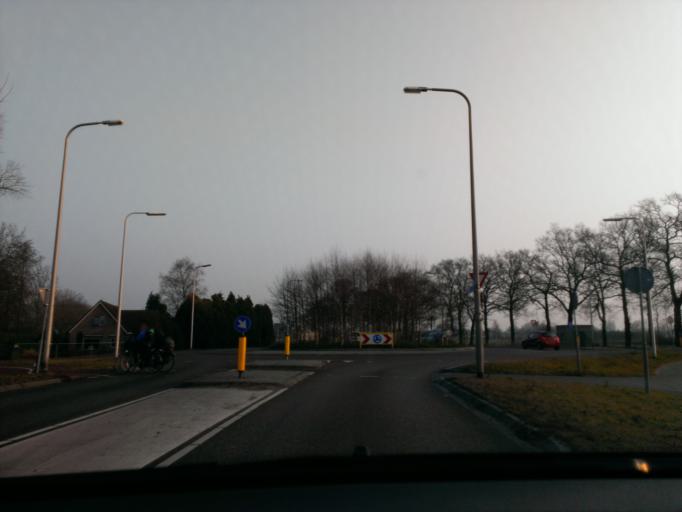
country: NL
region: Drenthe
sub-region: Gemeente Hoogeveen
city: Hoogeveen
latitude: 52.7211
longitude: 6.5197
